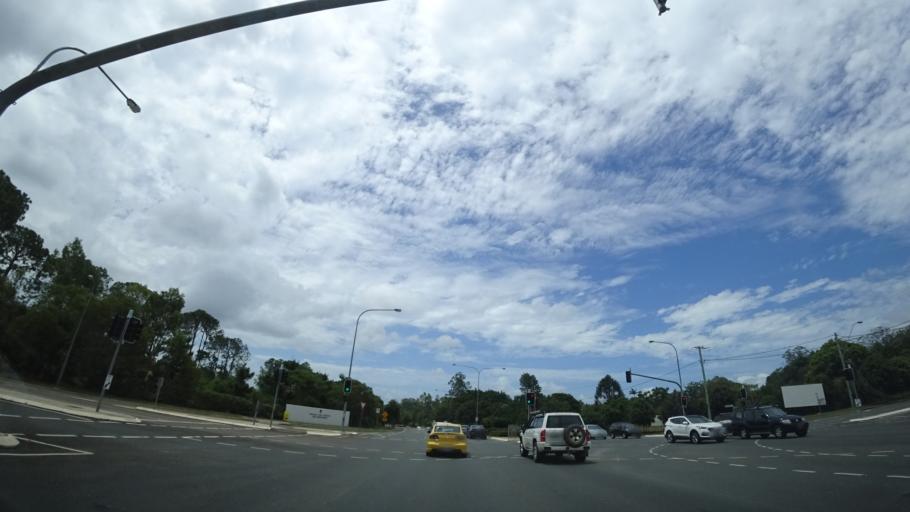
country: AU
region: Queensland
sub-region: Brisbane
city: Bridegman Downs
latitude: -27.3531
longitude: 152.9953
